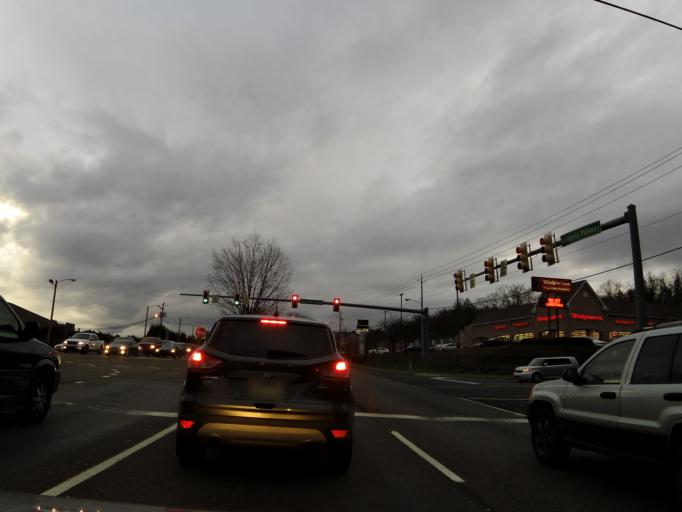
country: US
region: Tennessee
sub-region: Washington County
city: Johnson City
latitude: 36.3075
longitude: -82.3415
